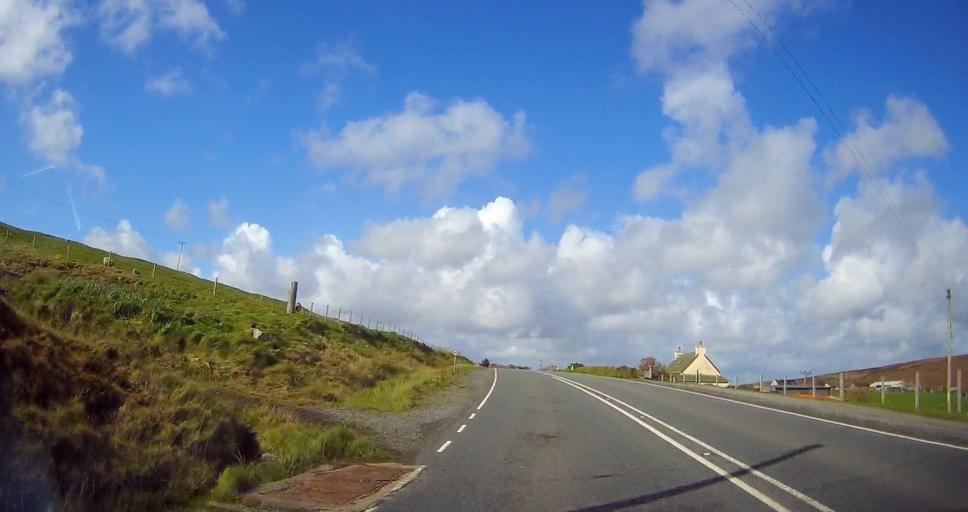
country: GB
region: Scotland
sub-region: Shetland Islands
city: Lerwick
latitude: 60.2372
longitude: -1.2307
